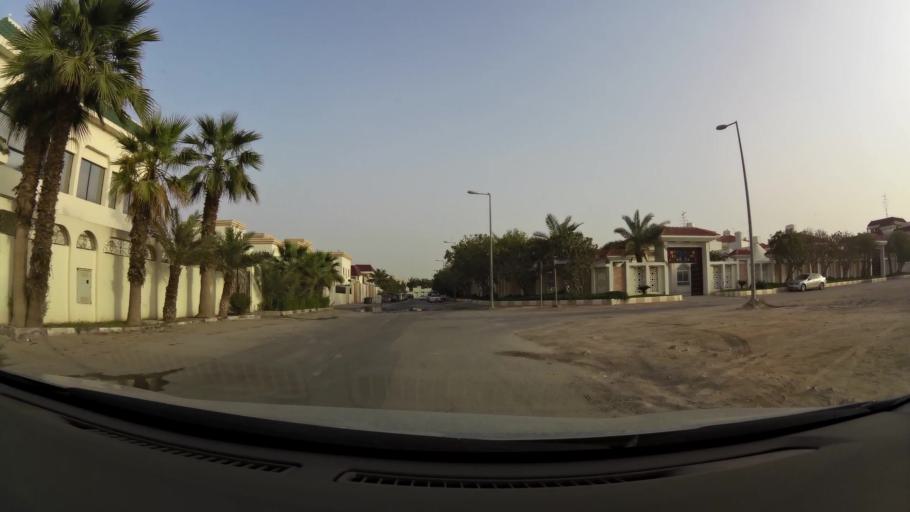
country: QA
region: Baladiyat ar Rayyan
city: Ar Rayyan
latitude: 25.2408
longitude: 51.4524
